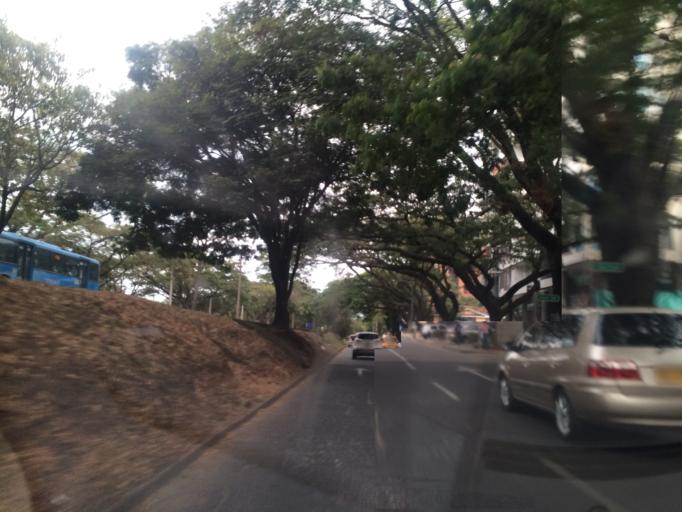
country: CO
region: Valle del Cauca
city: Cali
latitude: 3.3701
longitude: -76.5355
